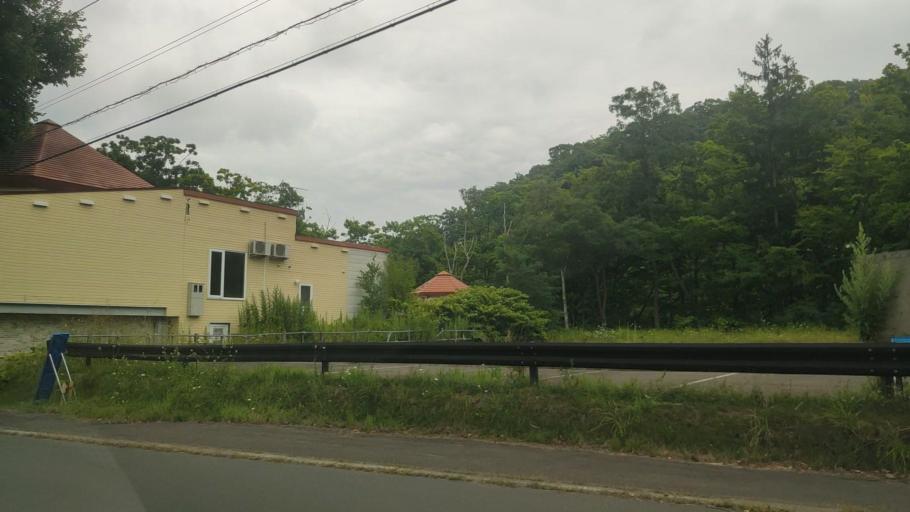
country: JP
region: Hokkaido
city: Sapporo
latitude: 42.9714
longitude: 141.1726
